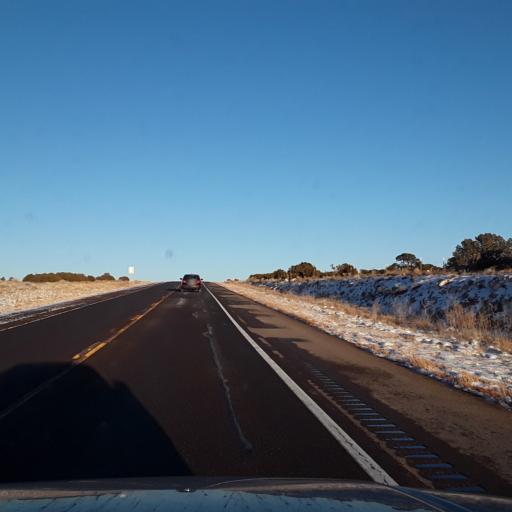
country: US
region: New Mexico
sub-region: Lincoln County
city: Carrizozo
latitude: 34.2338
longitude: -105.6195
